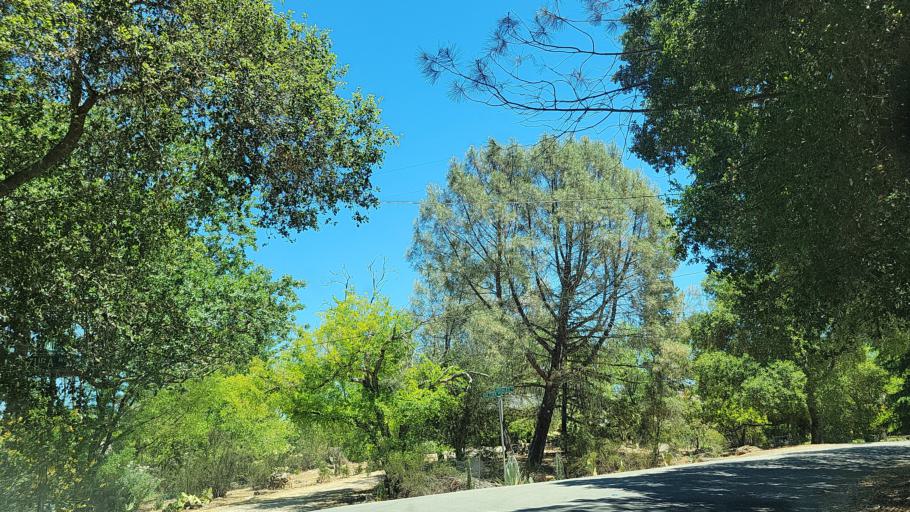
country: US
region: California
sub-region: San Luis Obispo County
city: Atascadero
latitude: 35.4976
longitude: -120.6731
